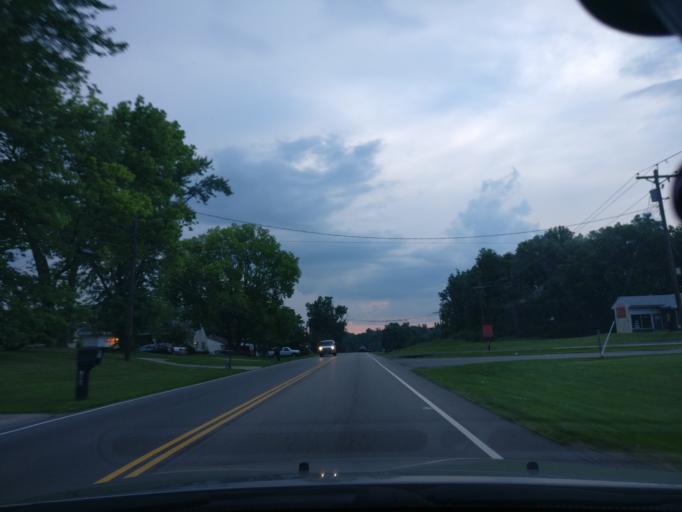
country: US
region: Ohio
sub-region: Warren County
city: Franklin
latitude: 39.5464
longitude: -84.2952
